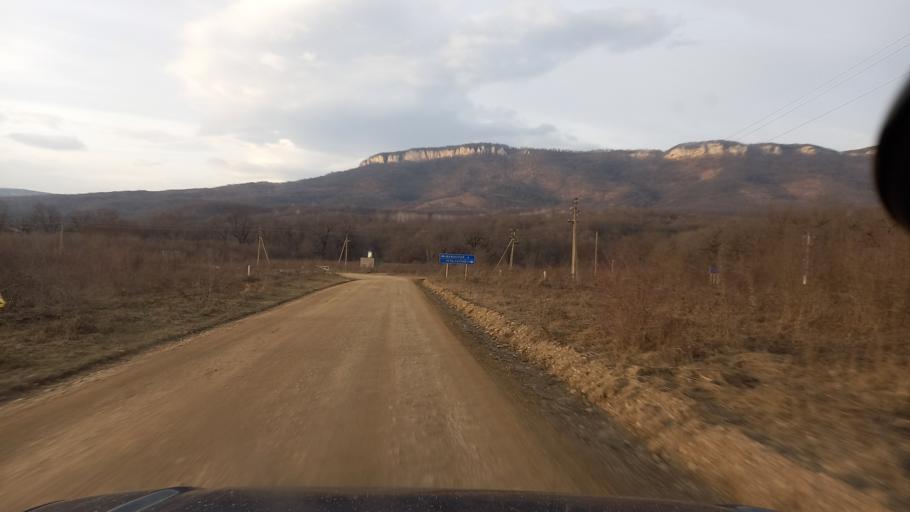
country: RU
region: Adygeya
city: Kamennomostskiy
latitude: 44.2116
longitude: 40.2529
